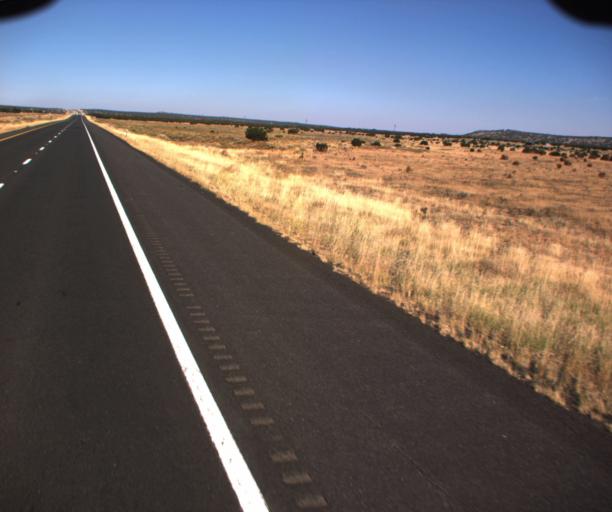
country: US
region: Arizona
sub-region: Coconino County
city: Flagstaff
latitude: 35.4444
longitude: -111.5645
